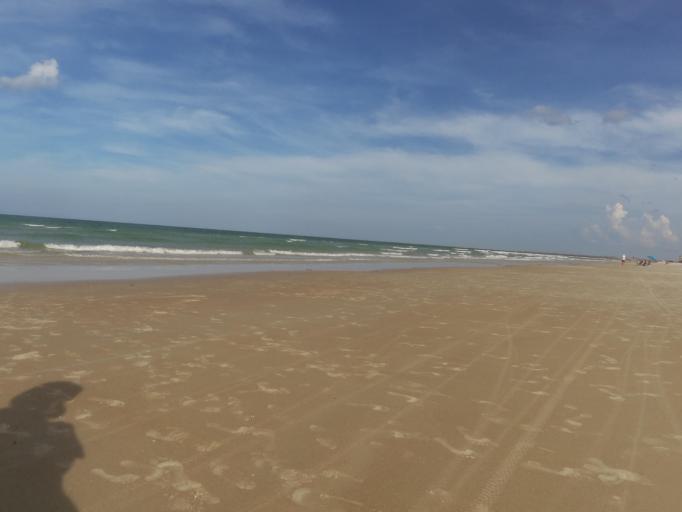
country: US
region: Florida
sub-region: Volusia County
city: Ponce Inlet
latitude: 29.0845
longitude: -80.9238
